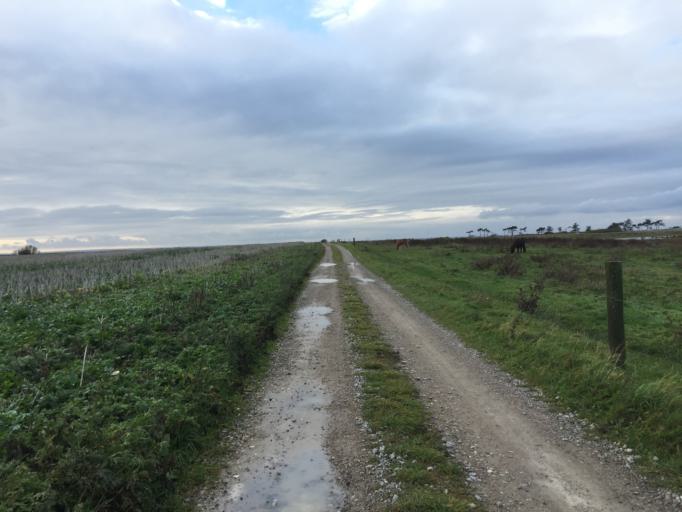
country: DK
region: Zealand
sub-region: Slagelse Kommune
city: Skaelskor
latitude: 55.2067
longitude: 11.1798
